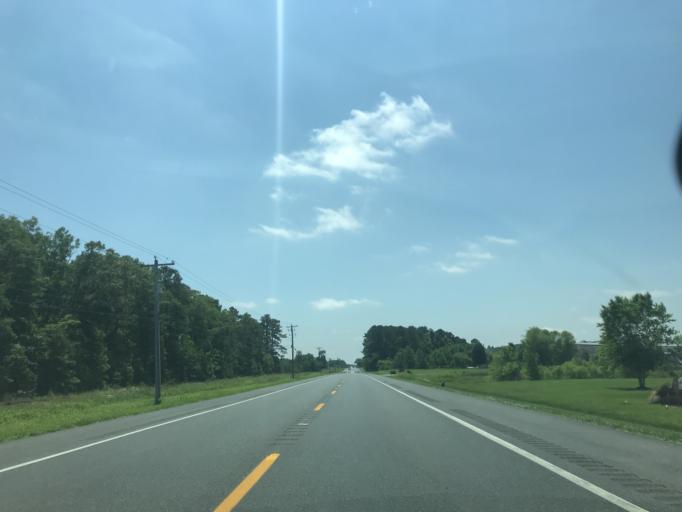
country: US
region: Maryland
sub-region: Dorchester County
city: Hurlock
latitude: 38.6219
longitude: -75.8811
